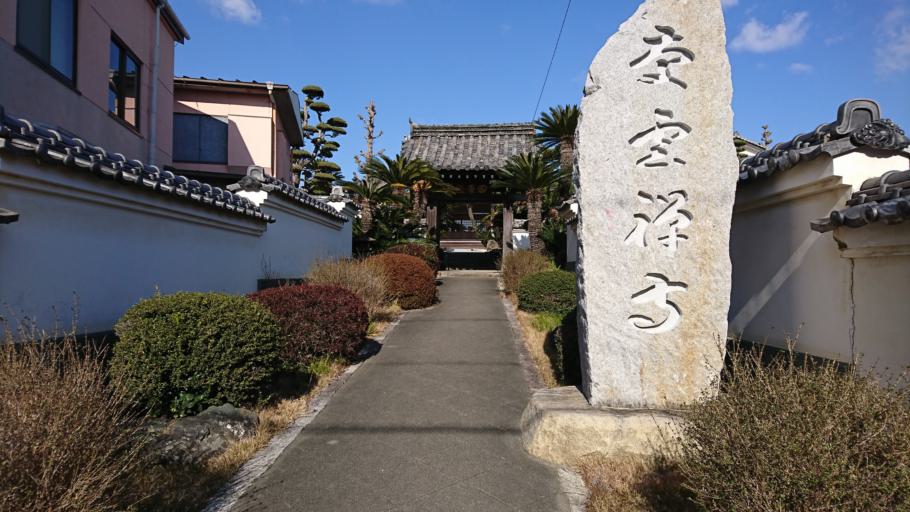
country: JP
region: Aichi
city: Tahara
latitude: 34.6676
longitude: 137.2667
